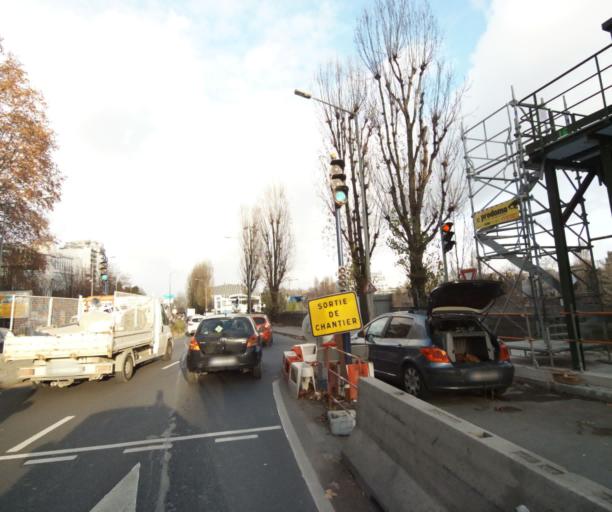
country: FR
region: Ile-de-France
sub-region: Departement des Hauts-de-Seine
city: Courbevoie
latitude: 48.8912
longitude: 2.2579
